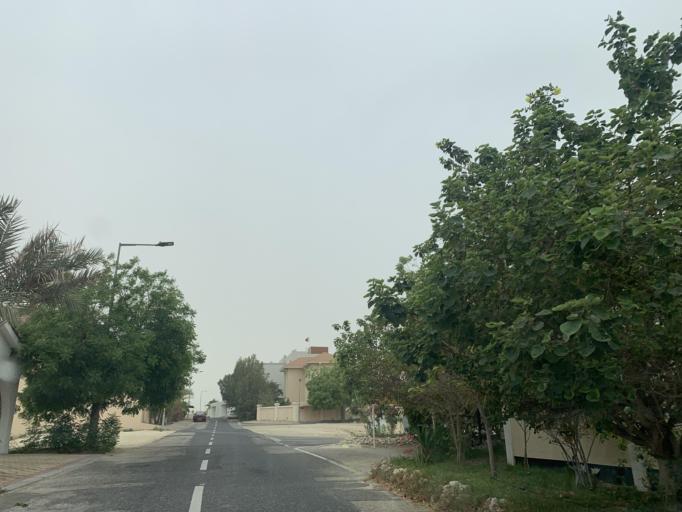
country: BH
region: Northern
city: Ar Rifa'
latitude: 26.1467
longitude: 50.5349
